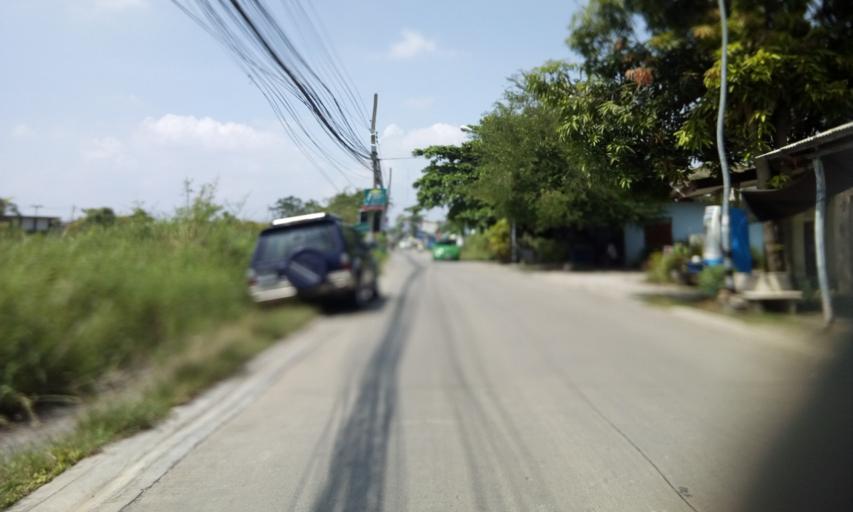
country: TH
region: Pathum Thani
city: Ban Rangsit
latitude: 14.0400
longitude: 100.7932
